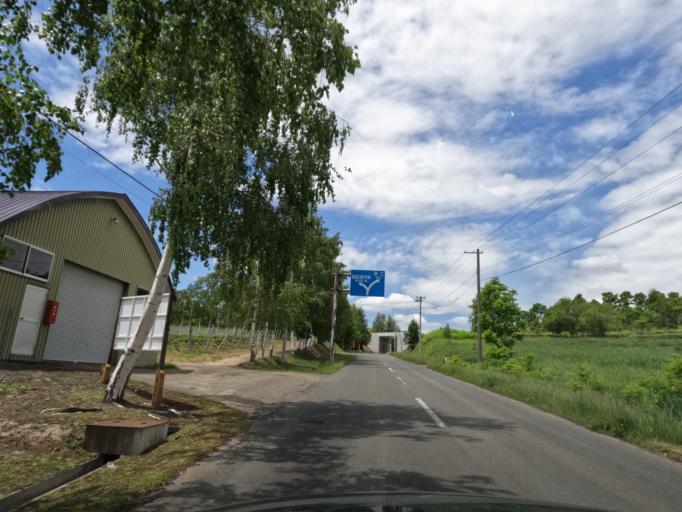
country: JP
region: Hokkaido
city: Shimo-furano
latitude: 43.3704
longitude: 142.3765
